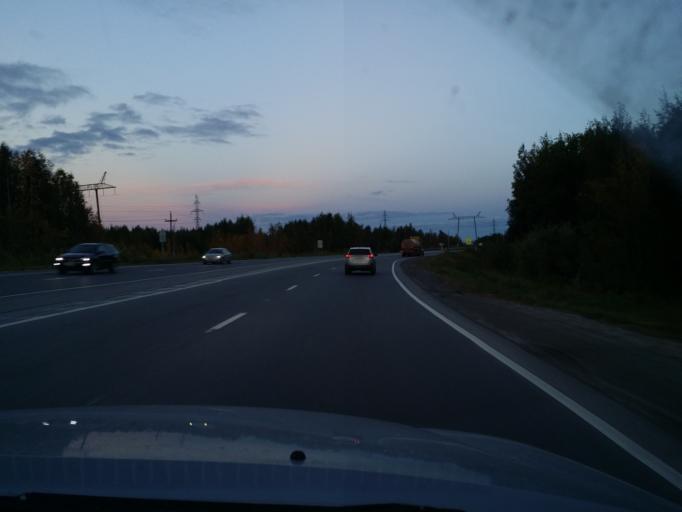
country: RU
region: Khanty-Mansiyskiy Avtonomnyy Okrug
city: Megion
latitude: 61.0499
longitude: 76.3375
